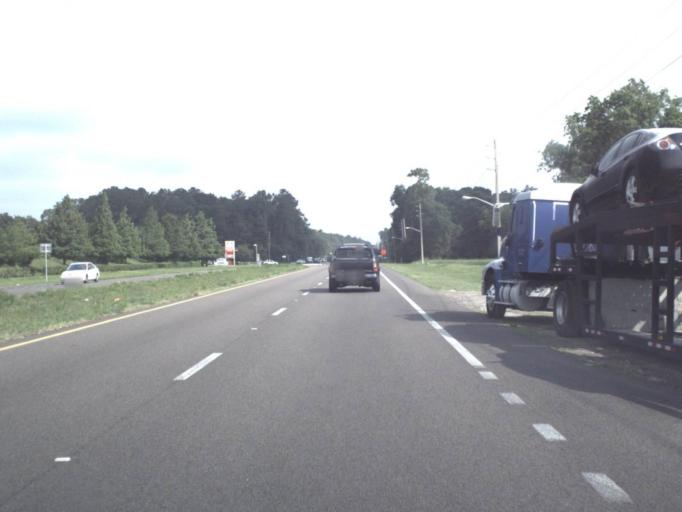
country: US
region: Florida
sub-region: Nassau County
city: Nassau Village-Ratliff
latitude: 30.4318
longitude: -81.7595
